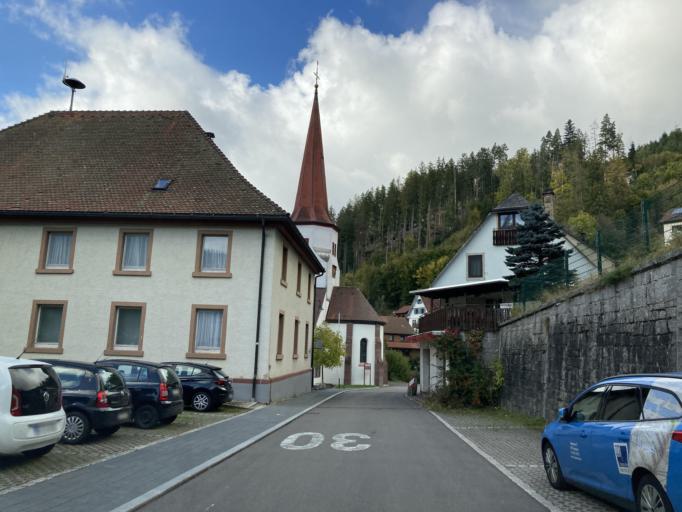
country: DE
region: Baden-Wuerttemberg
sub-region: Freiburg Region
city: Triberg im Schwarzwald
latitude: 48.1301
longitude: 8.2582
